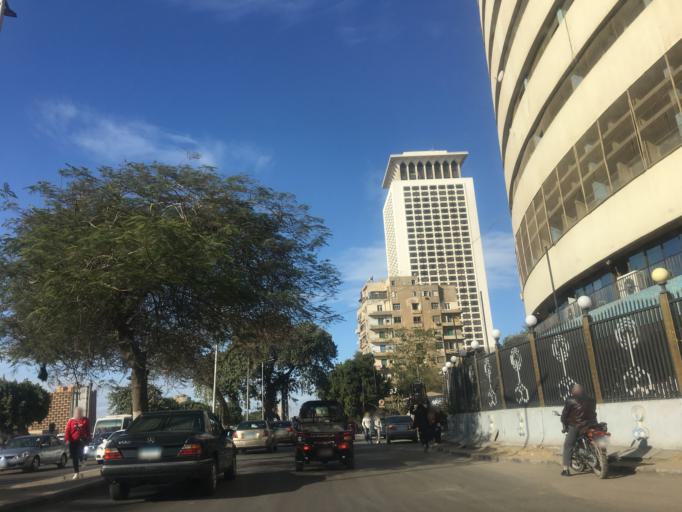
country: EG
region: Muhafazat al Qahirah
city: Cairo
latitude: 30.0529
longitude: 31.2303
